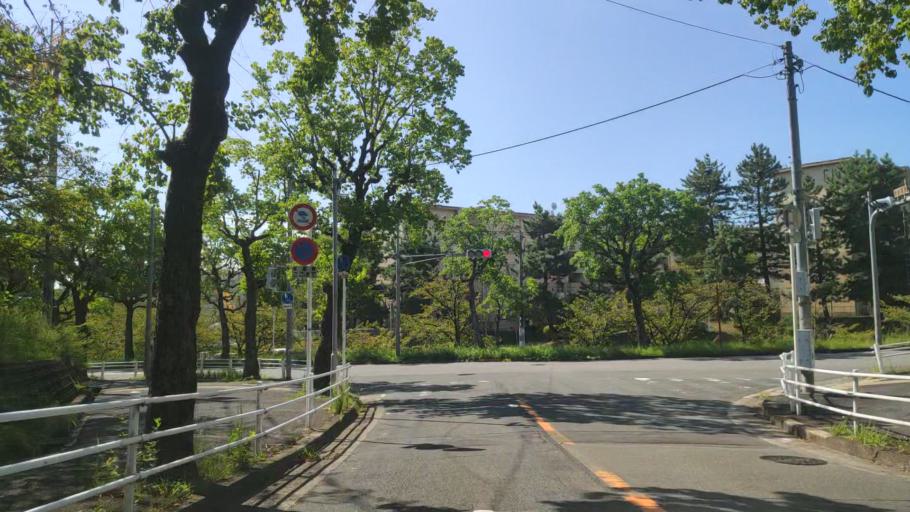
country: JP
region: Osaka
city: Mino
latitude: 34.8220
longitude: 135.5073
